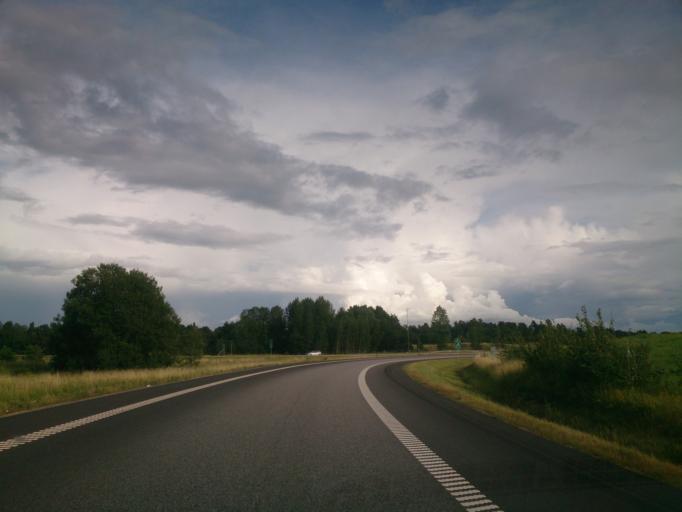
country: SE
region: OEstergoetland
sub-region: Linkopings Kommun
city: Ekangen
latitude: 58.4316
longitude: 15.6678
